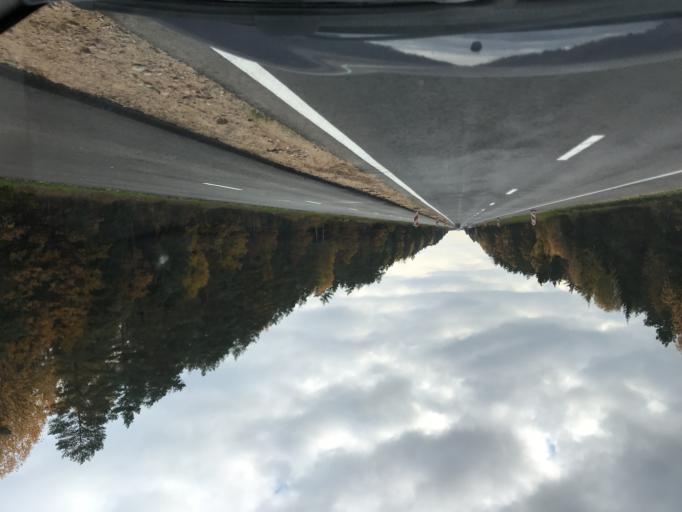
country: BY
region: Grodnenskaya
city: Lida
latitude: 53.8394
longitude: 25.1678
